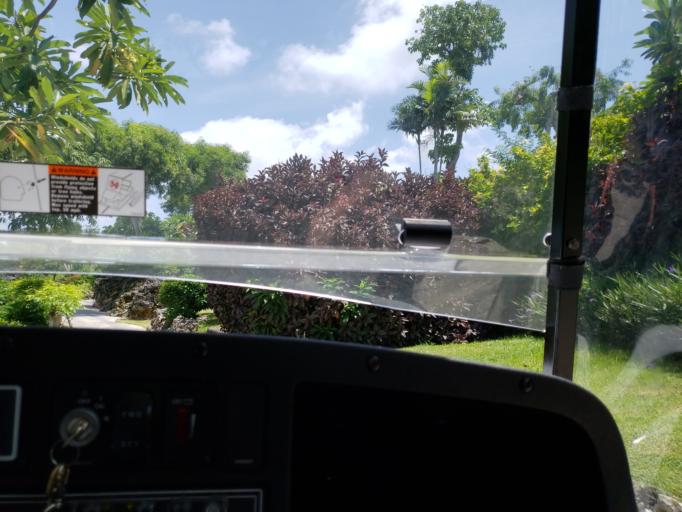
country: ID
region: Bali
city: Jimbaran
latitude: -8.7822
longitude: 115.1587
